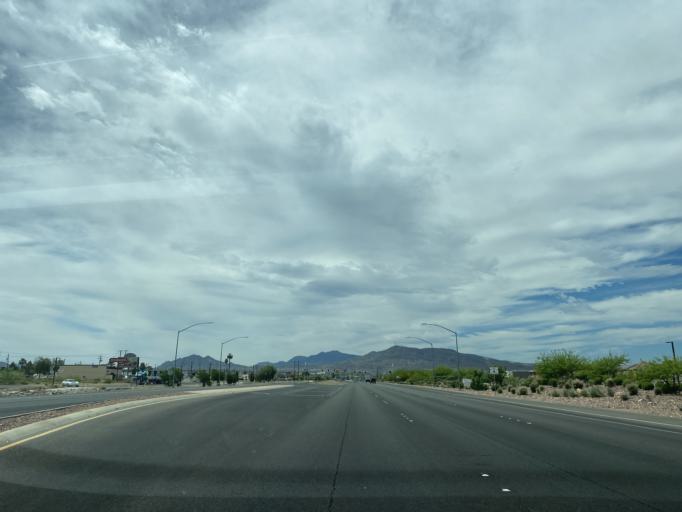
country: US
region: Nevada
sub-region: Clark County
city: Henderson
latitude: 36.0582
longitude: -114.9659
